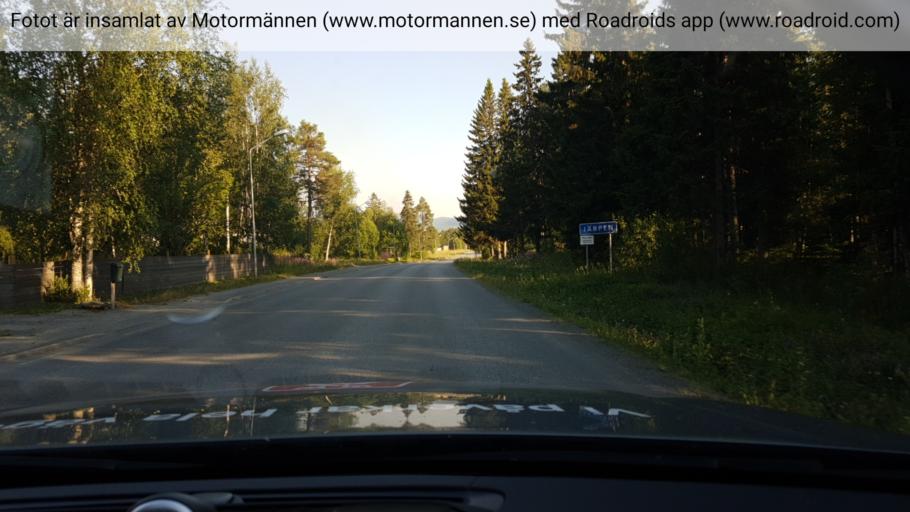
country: SE
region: Jaemtland
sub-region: Are Kommun
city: Jarpen
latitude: 63.3640
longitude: 13.4375
